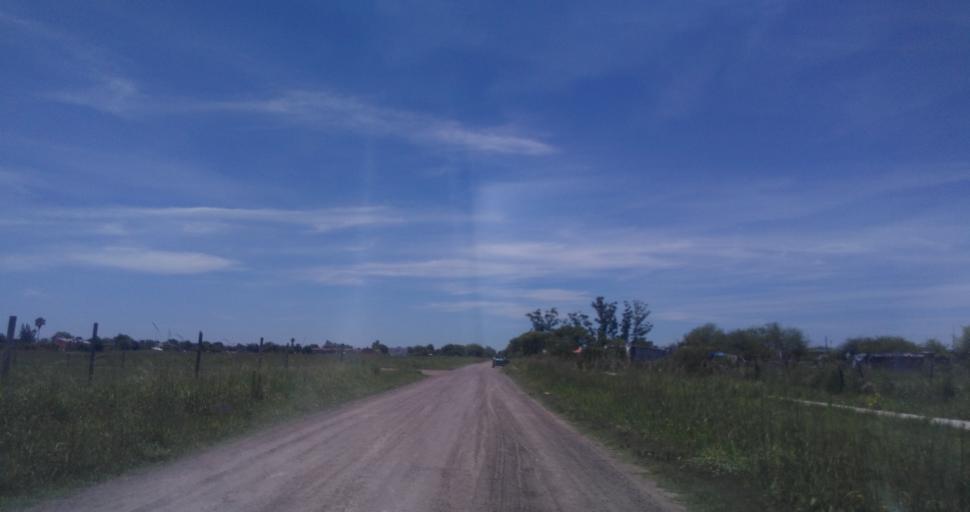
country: AR
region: Chaco
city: Fontana
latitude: -27.4245
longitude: -59.0446
